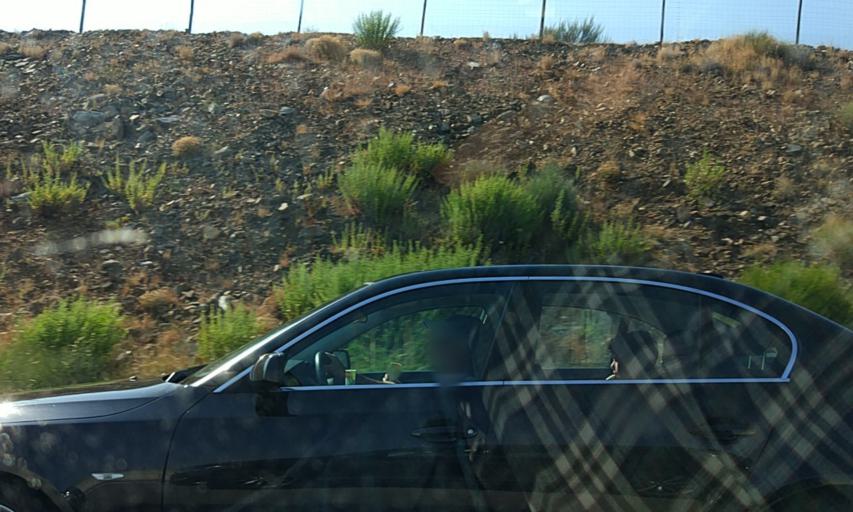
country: PT
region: Braganca
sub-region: Macedo de Cavaleiros
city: Macedo de Cavaleiros
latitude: 41.5501
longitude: -7.0374
